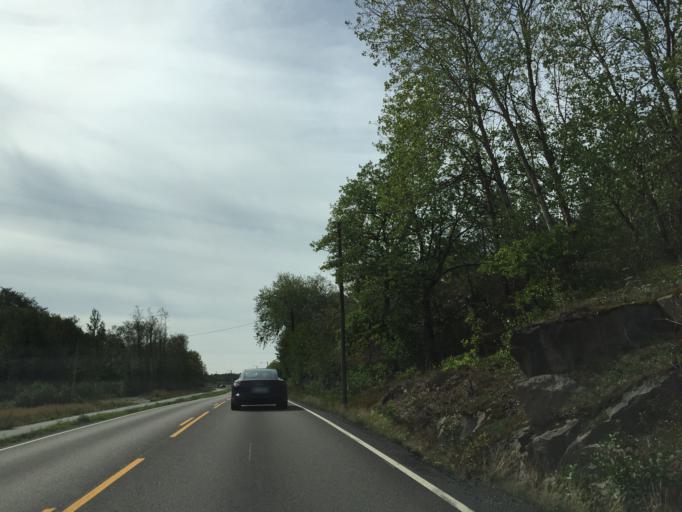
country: NO
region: Ostfold
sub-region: Fredrikstad
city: Fredrikstad
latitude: 59.1654
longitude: 10.9293
